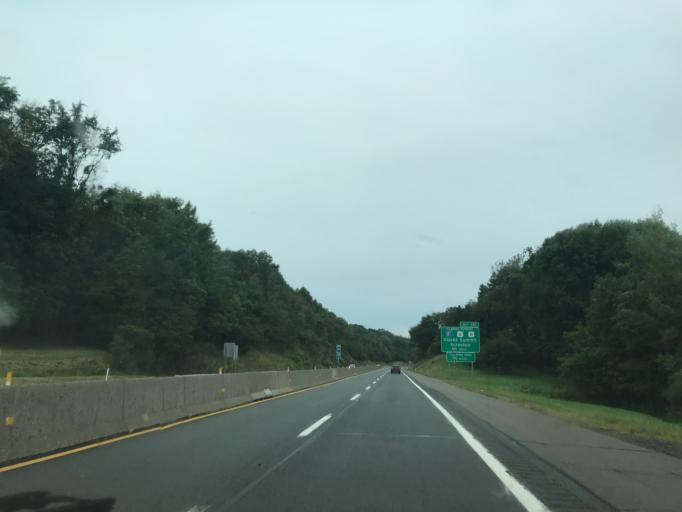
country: US
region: Pennsylvania
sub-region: Lackawanna County
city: Chinchilla
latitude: 41.4650
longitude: -75.6967
